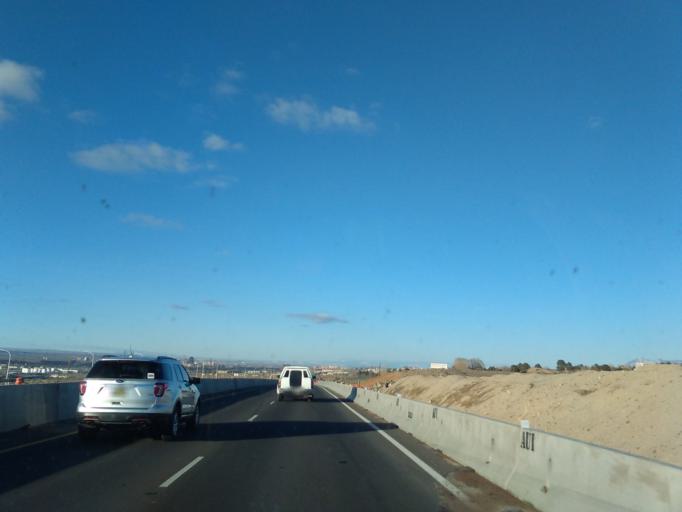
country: US
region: New Mexico
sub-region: Bernalillo County
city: South Valley
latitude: 35.0243
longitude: -106.6383
